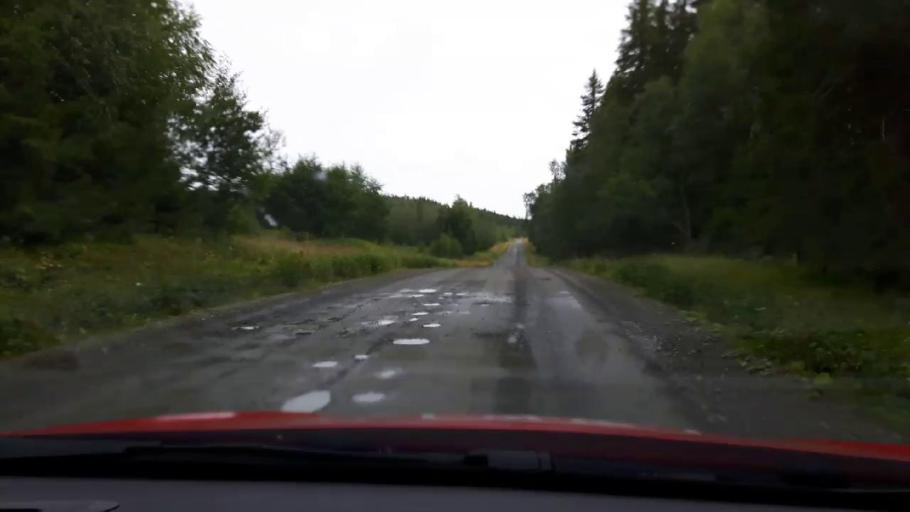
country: SE
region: Jaemtland
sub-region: Are Kommun
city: Are
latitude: 63.7440
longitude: 12.9842
